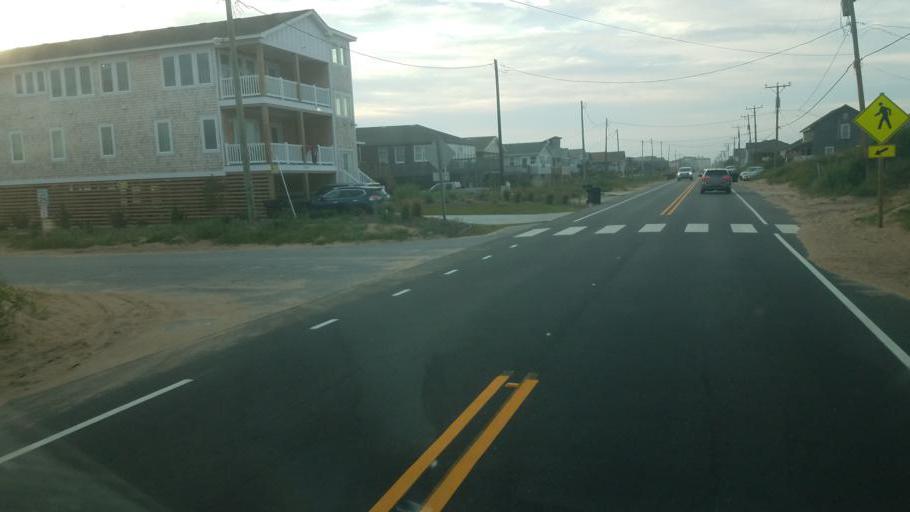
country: US
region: North Carolina
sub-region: Dare County
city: Kitty Hawk
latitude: 36.0895
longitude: -75.7047
